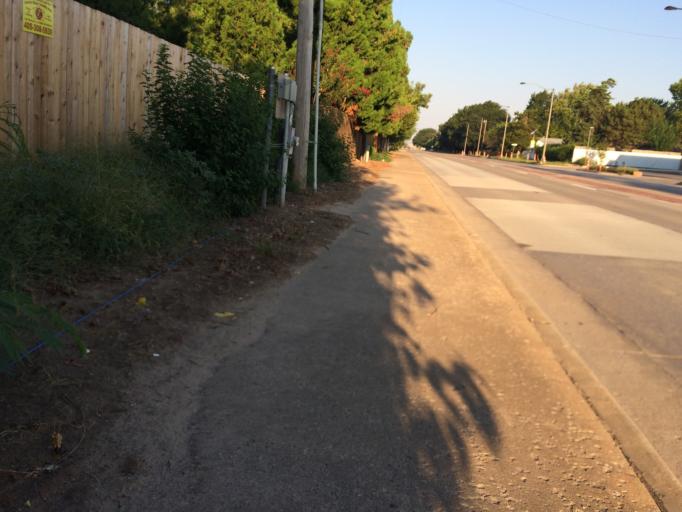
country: US
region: Oklahoma
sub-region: Cleveland County
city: Norman
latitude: 35.2184
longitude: -97.4614
